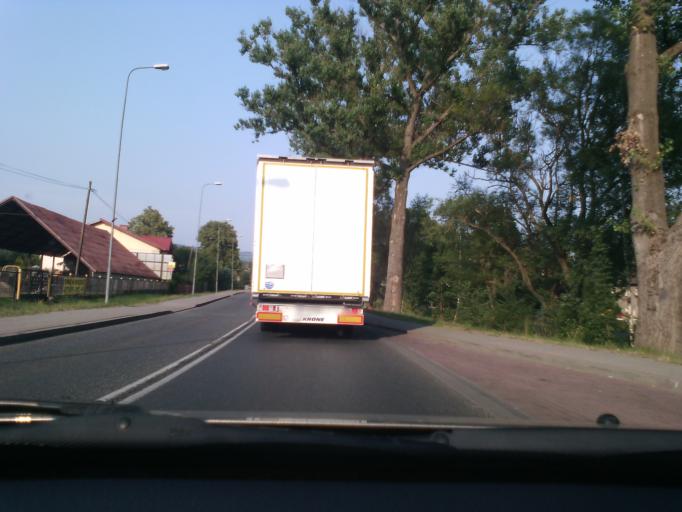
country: PL
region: Lower Silesian Voivodeship
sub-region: Powiat jeleniogorski
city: Jezow Sudecki
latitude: 50.9100
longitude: 15.8135
